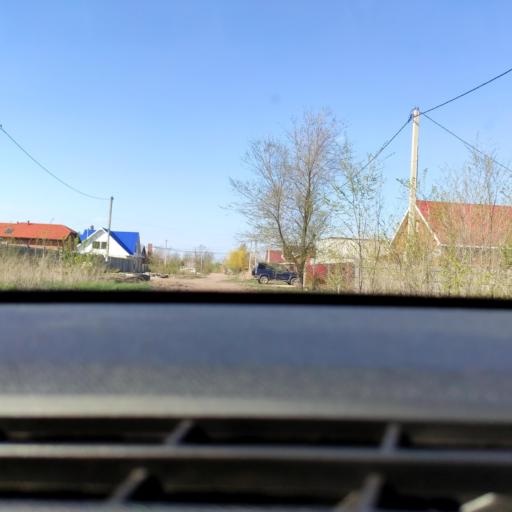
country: RU
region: Samara
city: Tol'yatti
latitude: 53.5552
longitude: 49.3815
